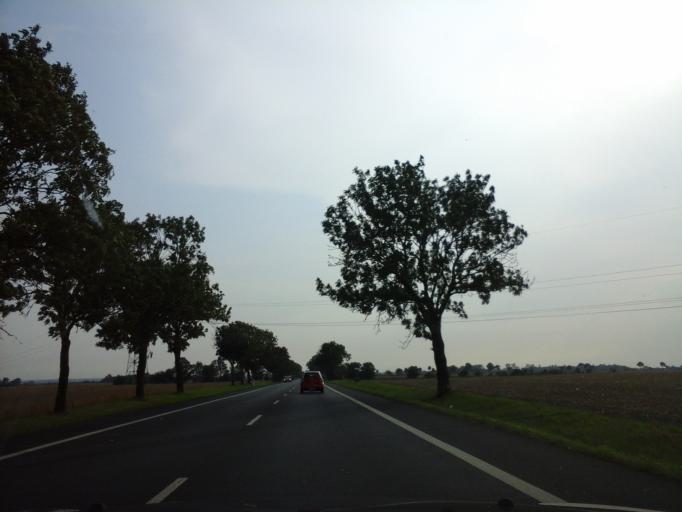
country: PL
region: Greater Poland Voivodeship
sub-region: Powiat koscianski
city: Koscian
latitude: 52.0653
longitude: 16.6032
